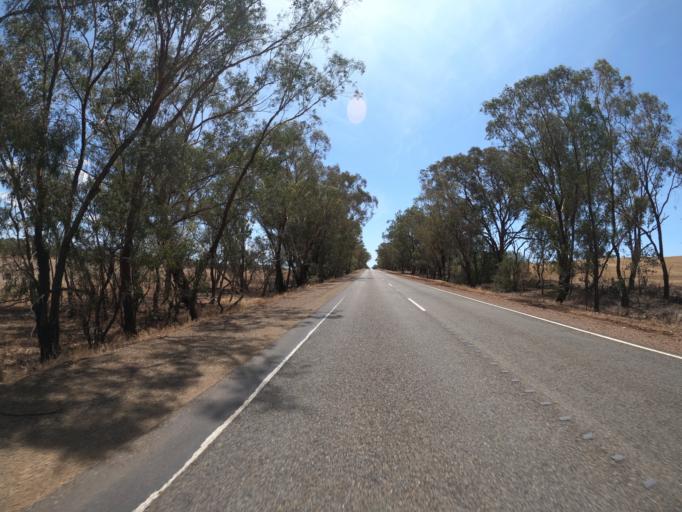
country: AU
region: Victoria
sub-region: Benalla
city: Benalla
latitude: -36.3527
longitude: 145.9637
